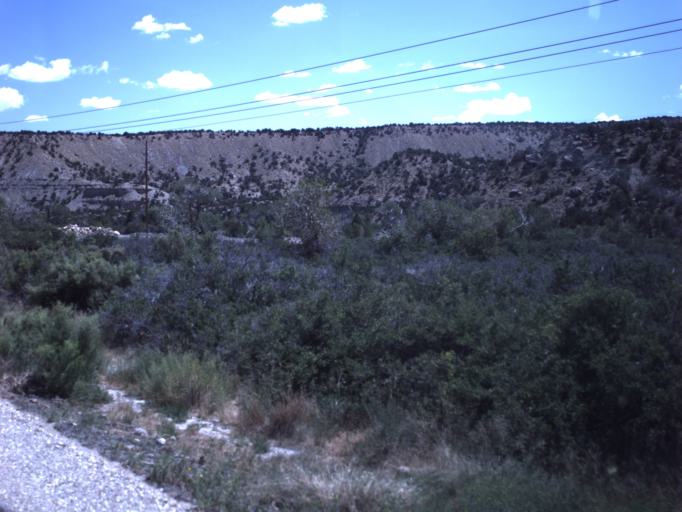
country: US
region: Utah
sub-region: Emery County
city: Orangeville
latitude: 39.2688
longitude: -111.1433
